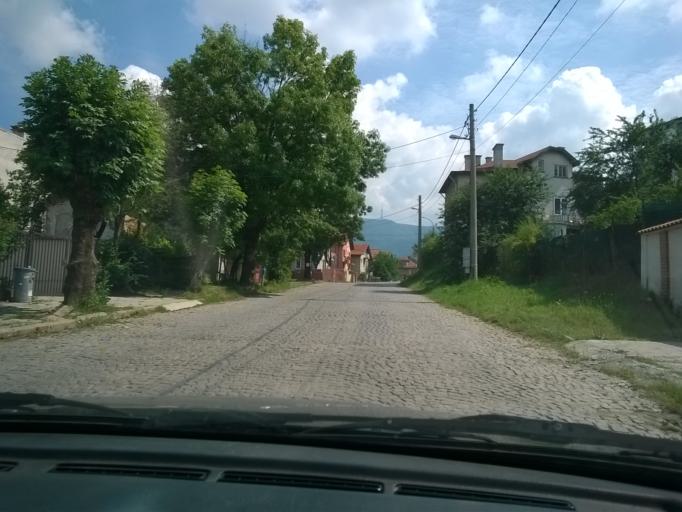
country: BG
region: Sofiya
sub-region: Obshtina Bozhurishte
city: Bozhurishte
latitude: 42.6783
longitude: 23.2409
